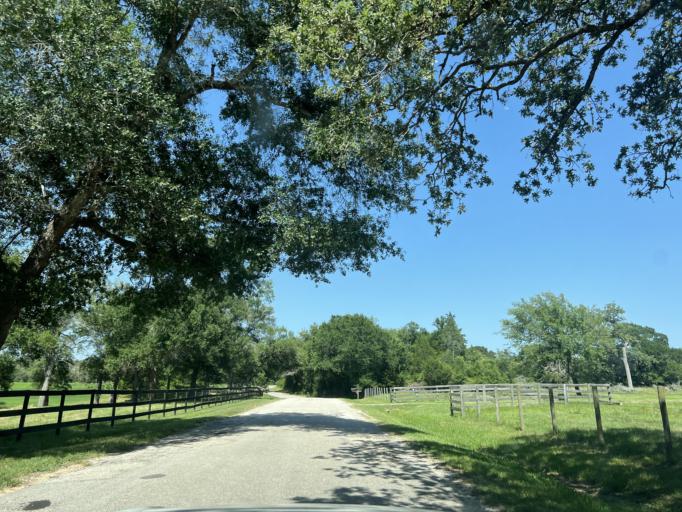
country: US
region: Texas
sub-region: Washington County
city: Brenham
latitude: 30.1784
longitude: -96.4937
